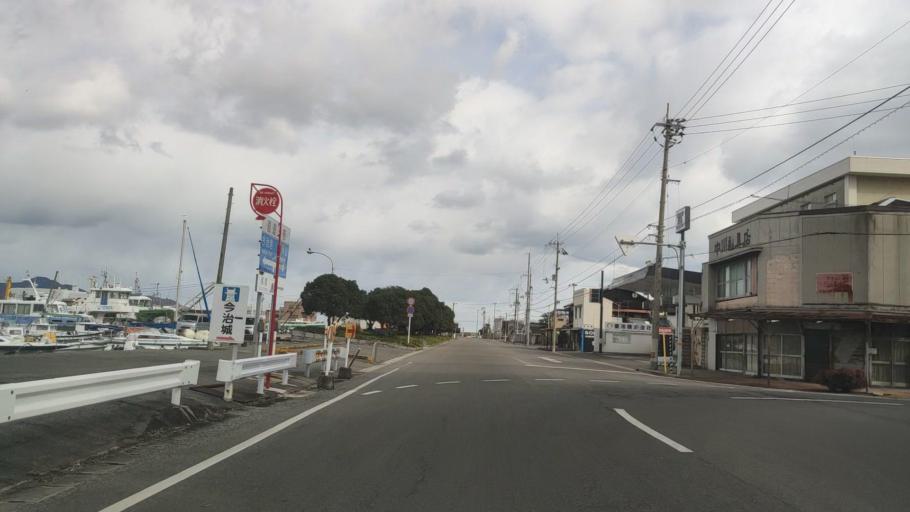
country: JP
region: Ehime
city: Saijo
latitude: 34.0659
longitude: 133.0069
